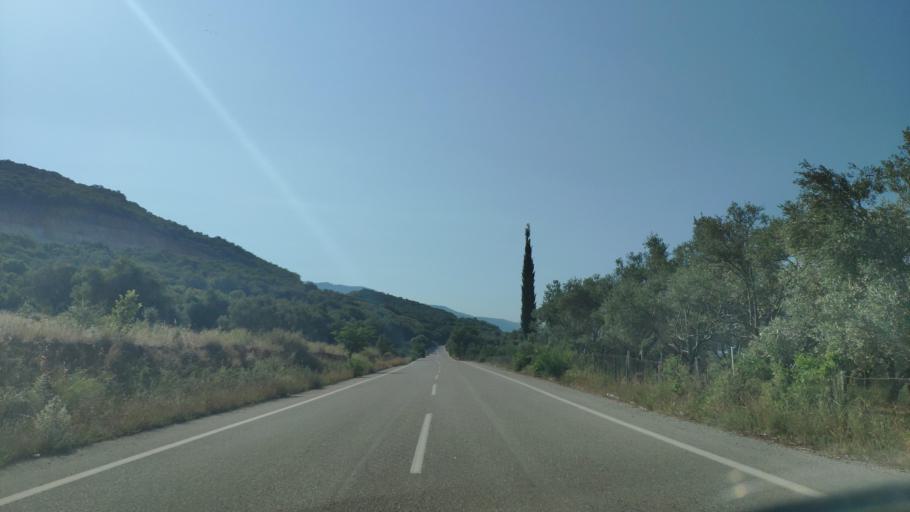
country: GR
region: West Greece
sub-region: Nomos Aitolias kai Akarnanias
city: Stanos
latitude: 38.7751
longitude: 21.1514
